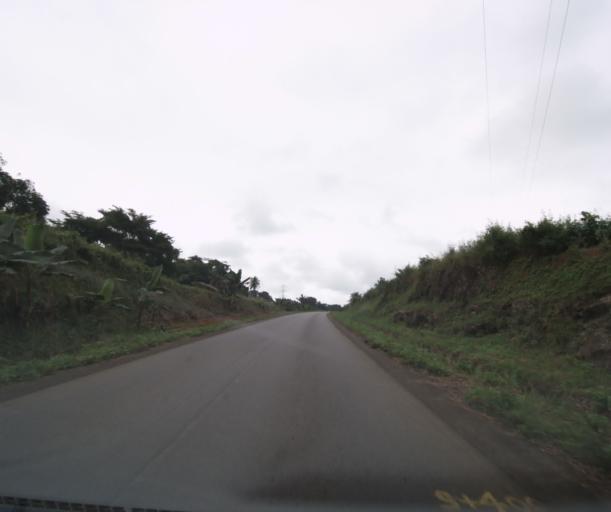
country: CM
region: Littoral
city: Edea
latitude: 3.7152
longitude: 10.1081
